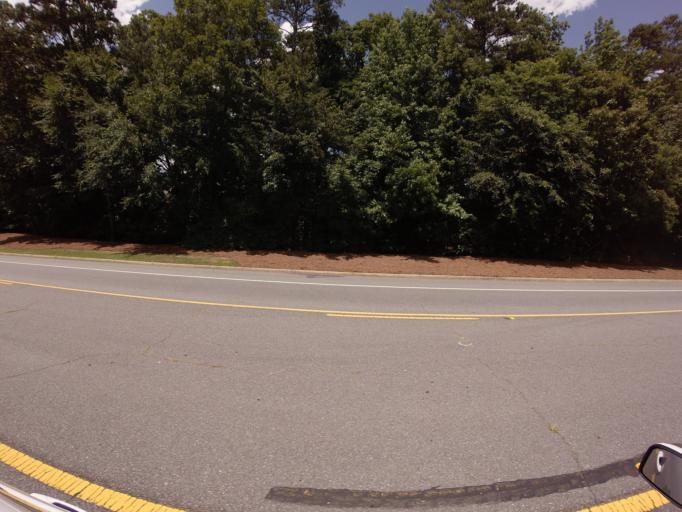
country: US
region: Georgia
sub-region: Fulton County
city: Johns Creek
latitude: 34.0085
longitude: -84.2156
